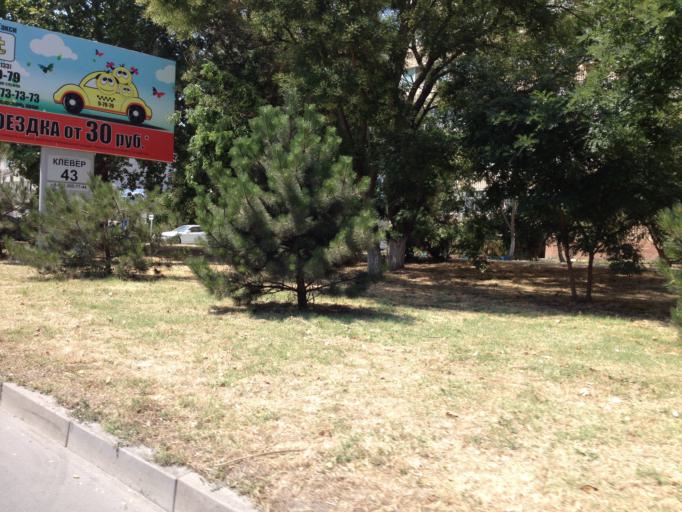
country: RU
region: Krasnodarskiy
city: Anapa
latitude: 44.8823
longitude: 37.3249
